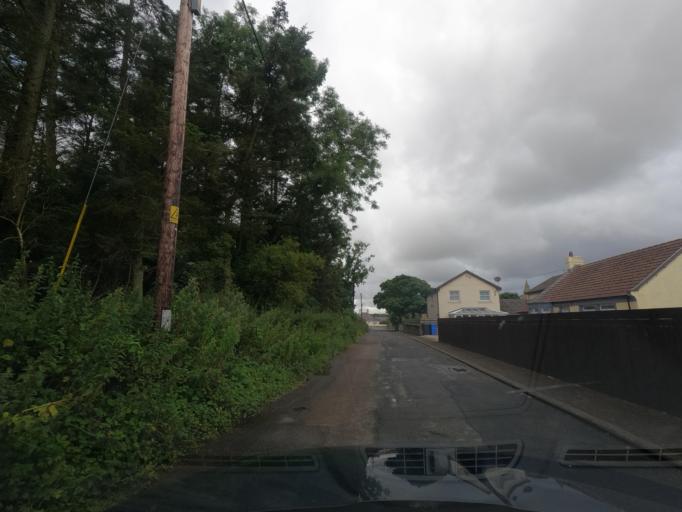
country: GB
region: England
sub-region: Northumberland
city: Ancroft
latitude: 55.7362
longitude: -1.9891
